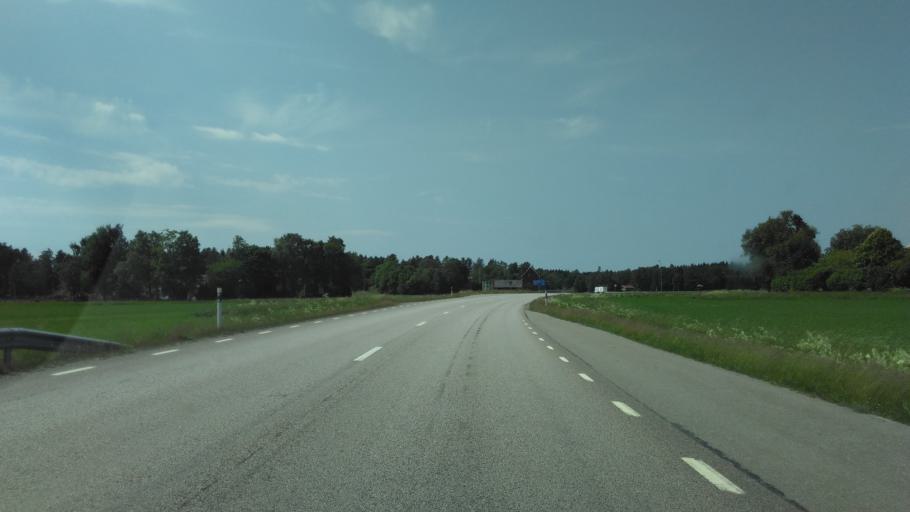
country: SE
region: Vaestra Goetaland
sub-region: Vara Kommun
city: Vara
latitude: 58.4385
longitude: 12.9401
